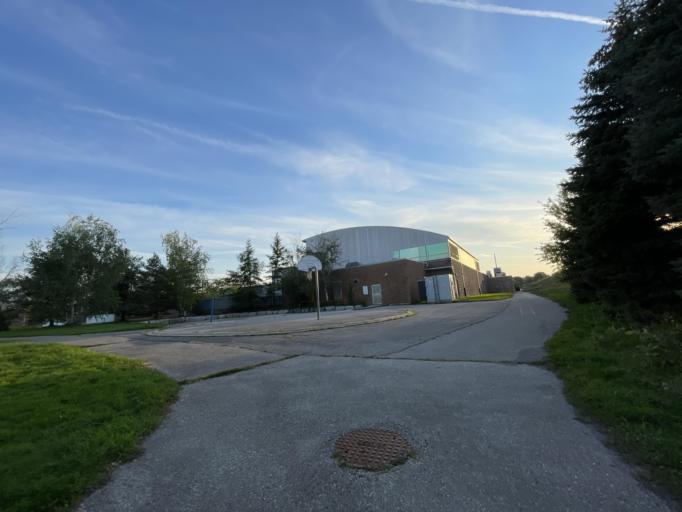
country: CA
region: Ontario
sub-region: Wellington County
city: Guelph
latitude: 43.5256
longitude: -80.2908
